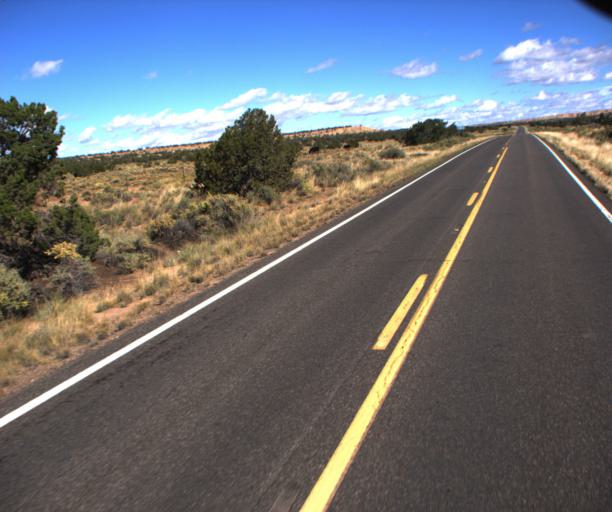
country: US
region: Arizona
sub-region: Apache County
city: Saint Johns
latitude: 34.7719
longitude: -109.2402
